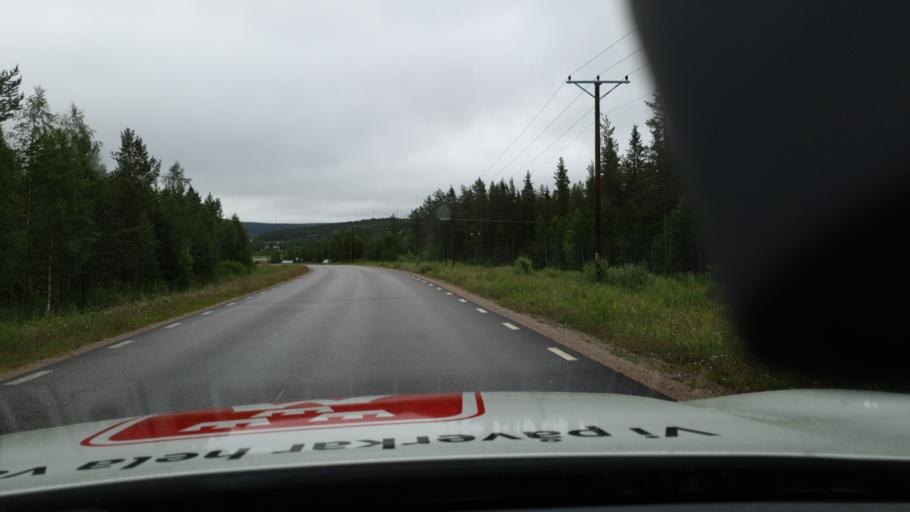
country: SE
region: Norrbotten
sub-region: Overtornea Kommun
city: OEvertornea
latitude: 66.3941
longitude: 23.6061
